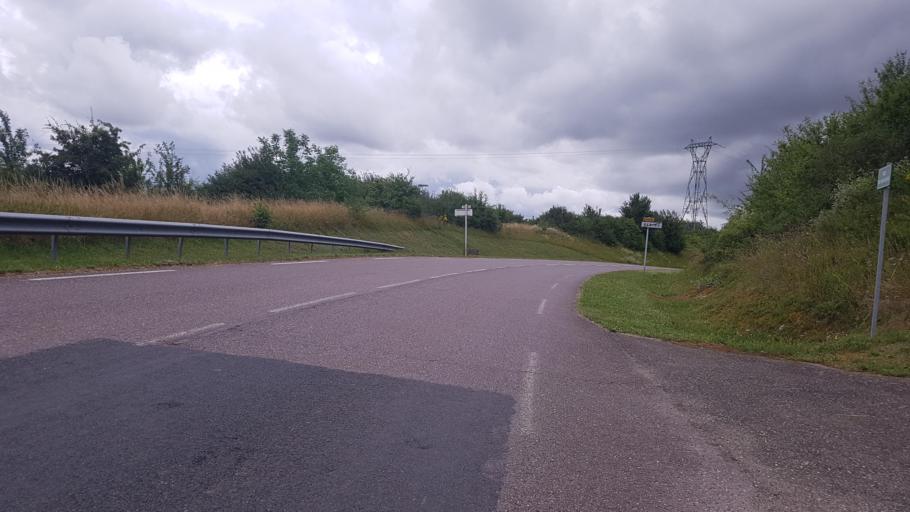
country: FR
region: Lorraine
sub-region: Departement de la Moselle
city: Lorquin
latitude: 48.7078
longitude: 6.9998
